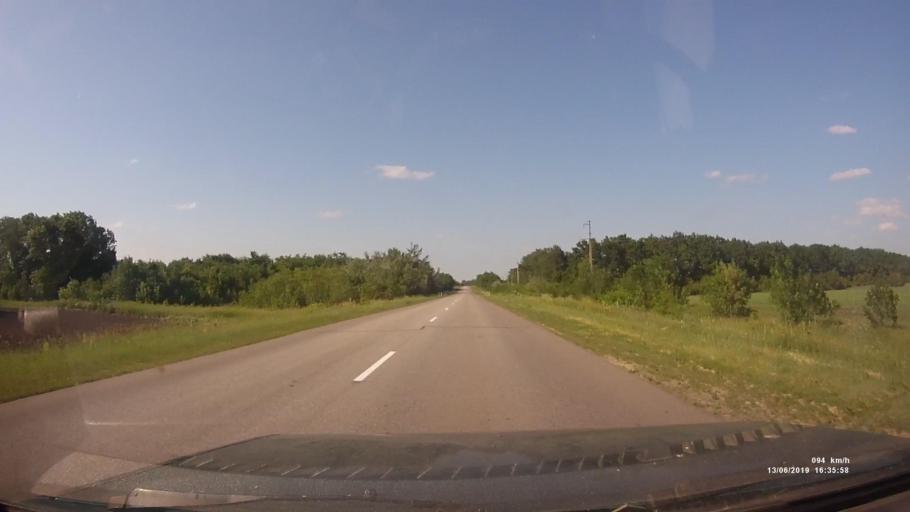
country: RU
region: Rostov
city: Kazanskaya
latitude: 49.8889
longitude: 41.3024
